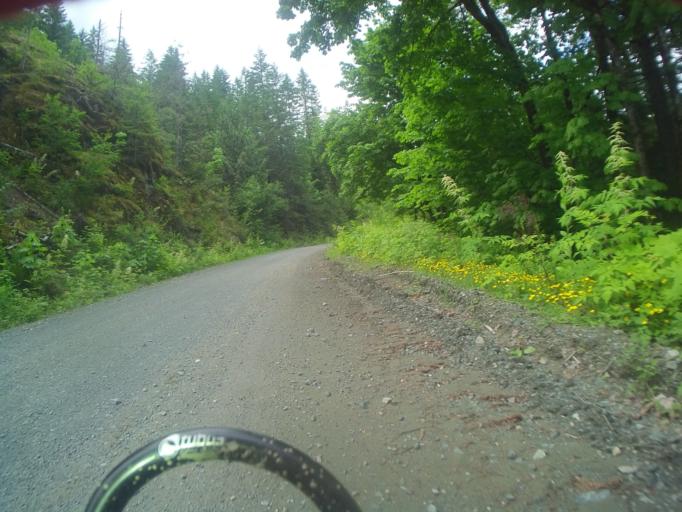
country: CA
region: British Columbia
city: Agassiz
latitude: 49.5945
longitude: -121.9336
